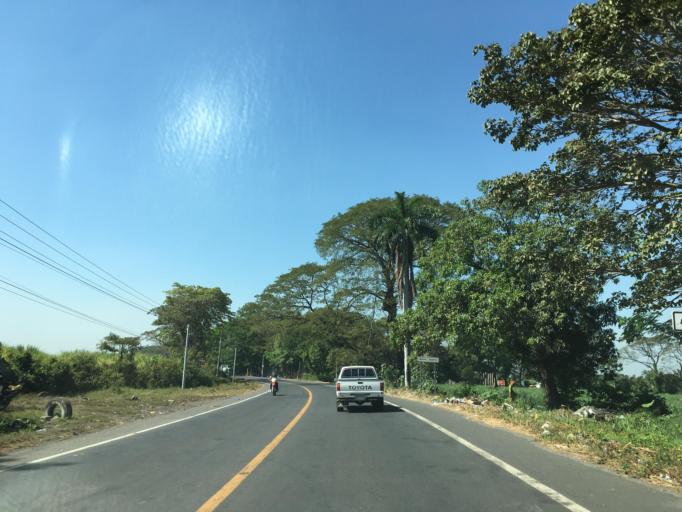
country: GT
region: Escuintla
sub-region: Municipio de Masagua
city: Masagua
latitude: 14.1982
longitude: -90.8528
